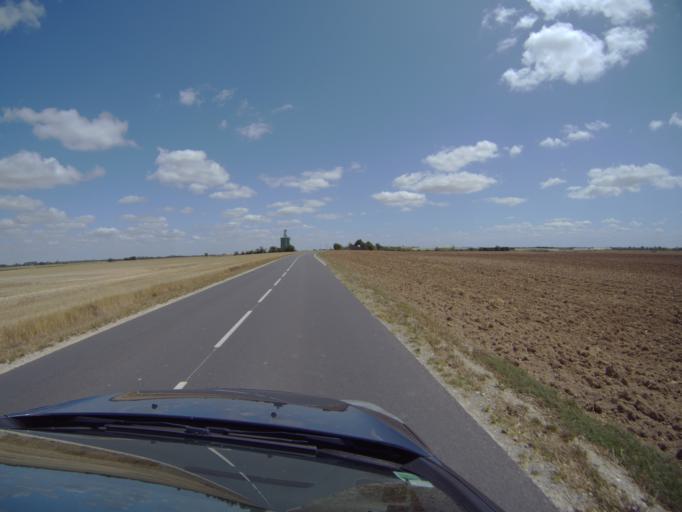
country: FR
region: Poitou-Charentes
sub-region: Departement de la Charente-Maritime
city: Marans
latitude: 46.2923
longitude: -0.9614
